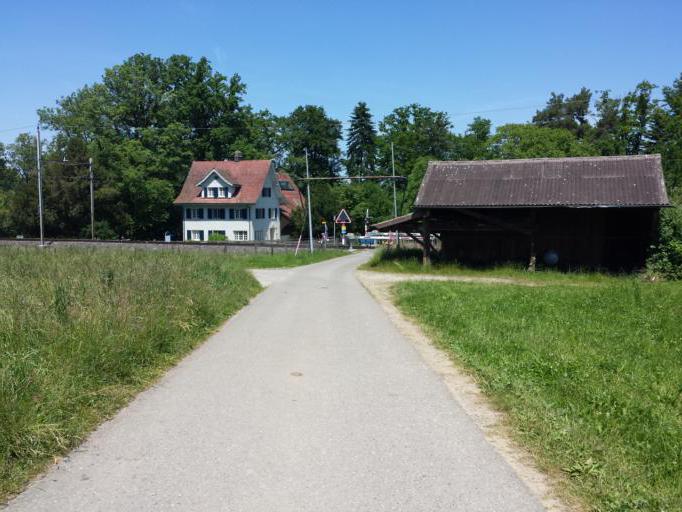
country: CH
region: Thurgau
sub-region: Arbon District
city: Uttwil
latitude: 47.5795
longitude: 9.3574
